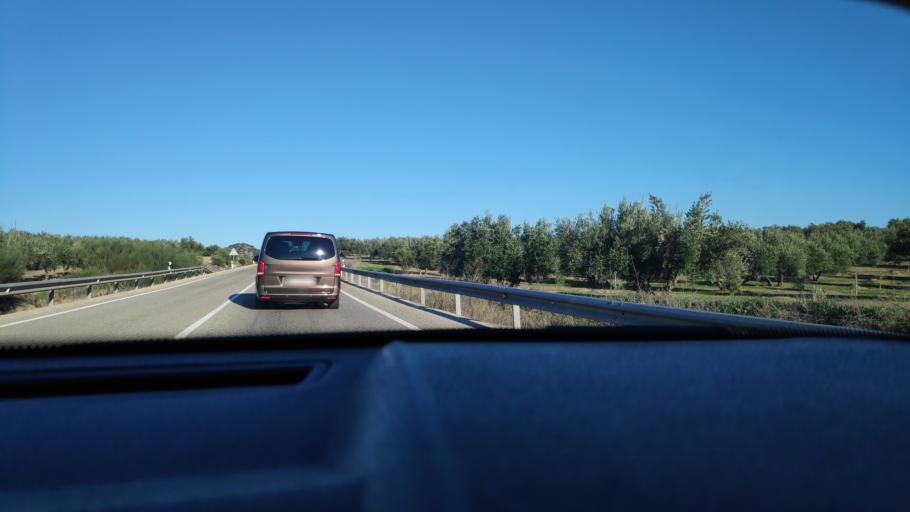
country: ES
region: Andalusia
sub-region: Province of Cordoba
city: Fuente-Tojar
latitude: 37.5641
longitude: -4.1850
